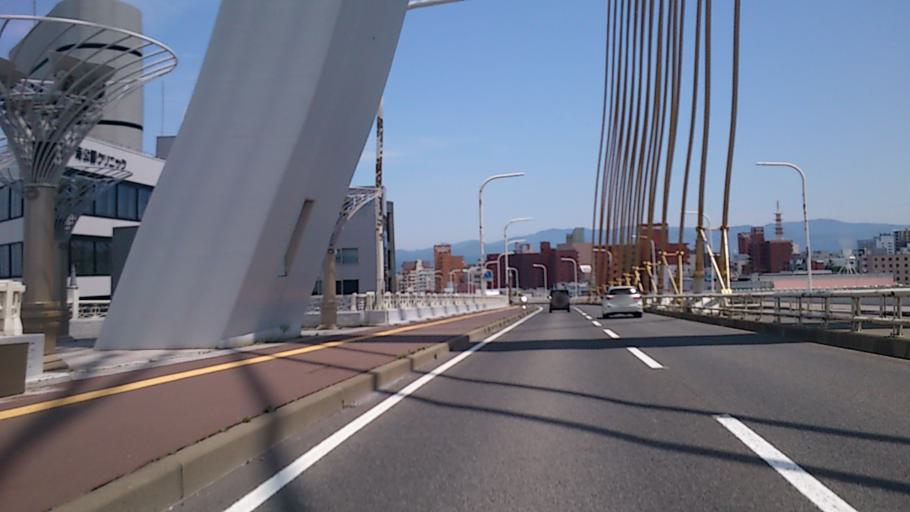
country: JP
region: Aomori
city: Aomori Shi
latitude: 40.8299
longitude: 140.7378
